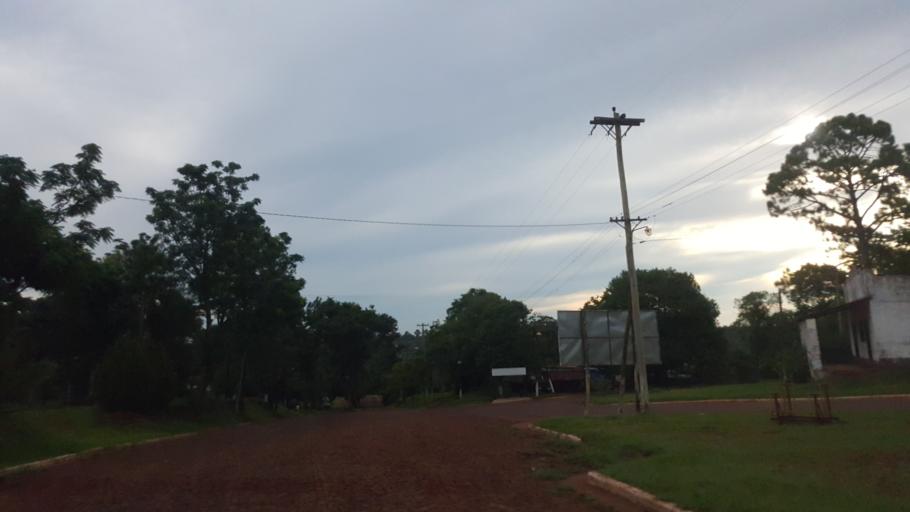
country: AR
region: Misiones
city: Santo Pipo
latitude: -27.1087
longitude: -55.3757
